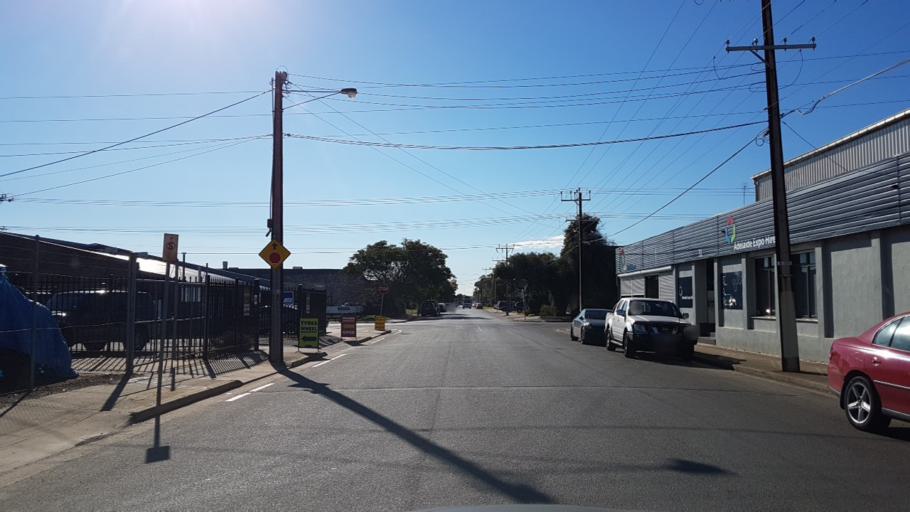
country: AU
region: South Australia
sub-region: City of West Torrens
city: Plympton
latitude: -34.9591
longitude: 138.5411
